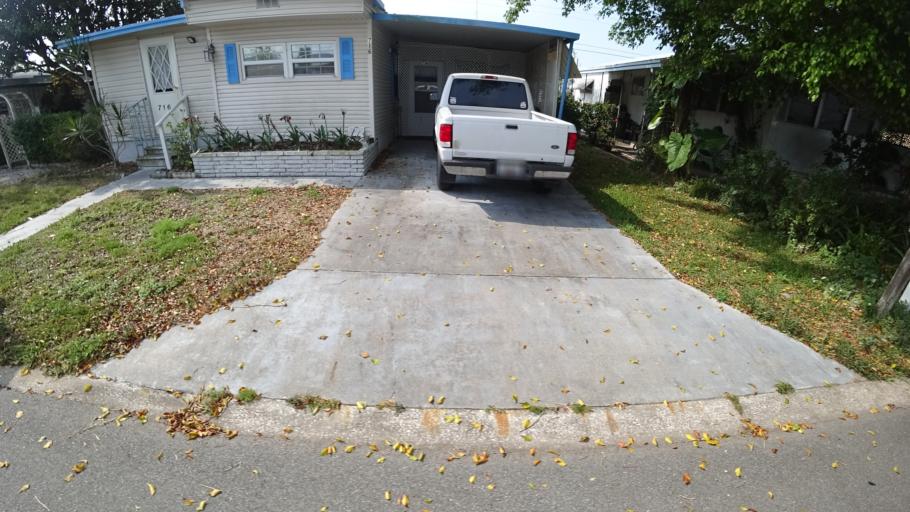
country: US
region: Florida
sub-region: Manatee County
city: South Bradenton
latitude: 27.4522
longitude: -82.5699
